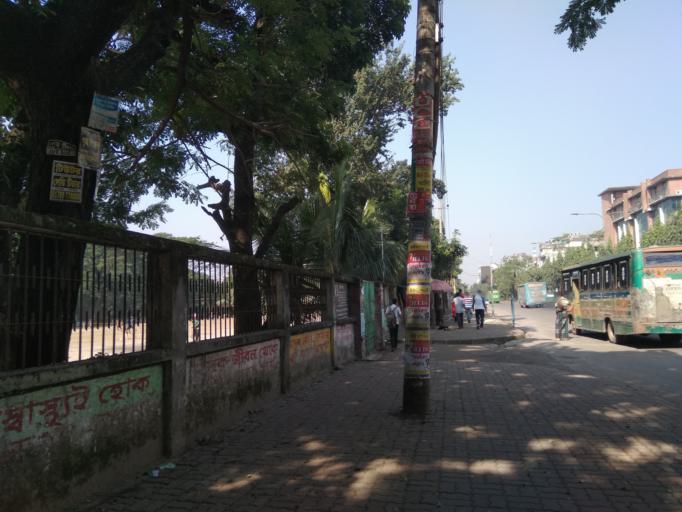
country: BD
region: Dhaka
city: Azimpur
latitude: 23.7486
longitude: 90.3797
